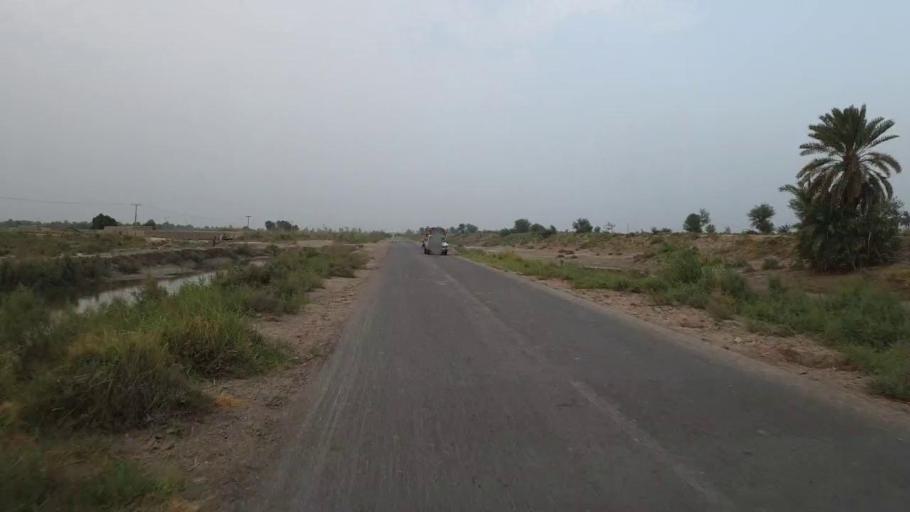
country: PK
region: Sindh
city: Daur
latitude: 26.4478
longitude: 68.2853
